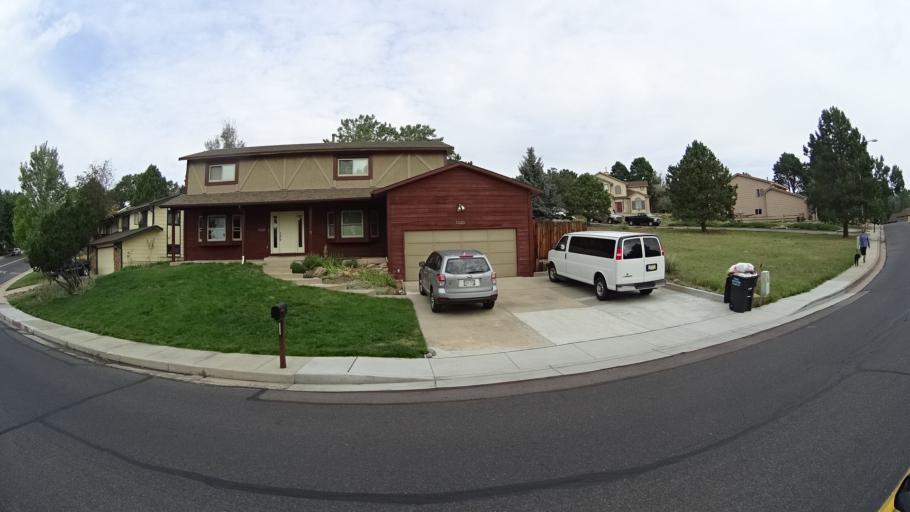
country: US
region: Colorado
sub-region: El Paso County
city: Air Force Academy
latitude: 38.9301
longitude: -104.8459
